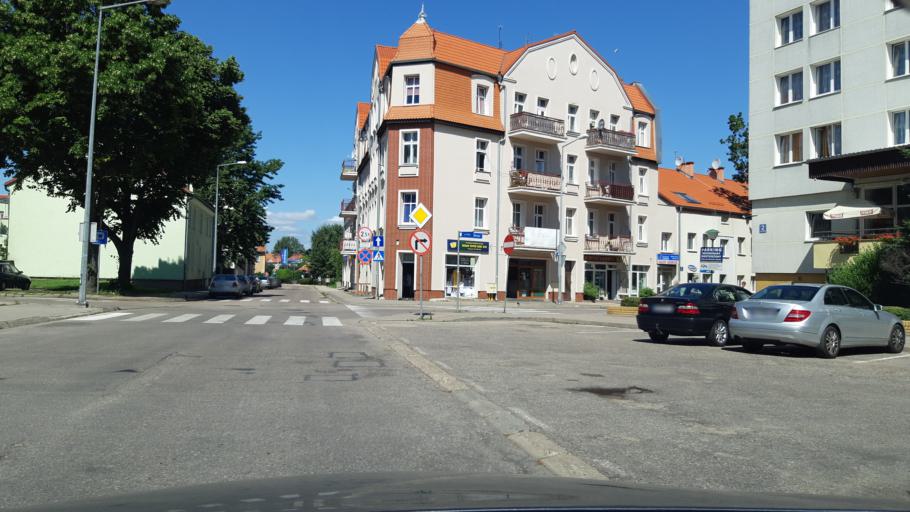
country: PL
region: Warmian-Masurian Voivodeship
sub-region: Powiat gizycki
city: Gizycko
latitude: 54.0371
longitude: 21.7676
